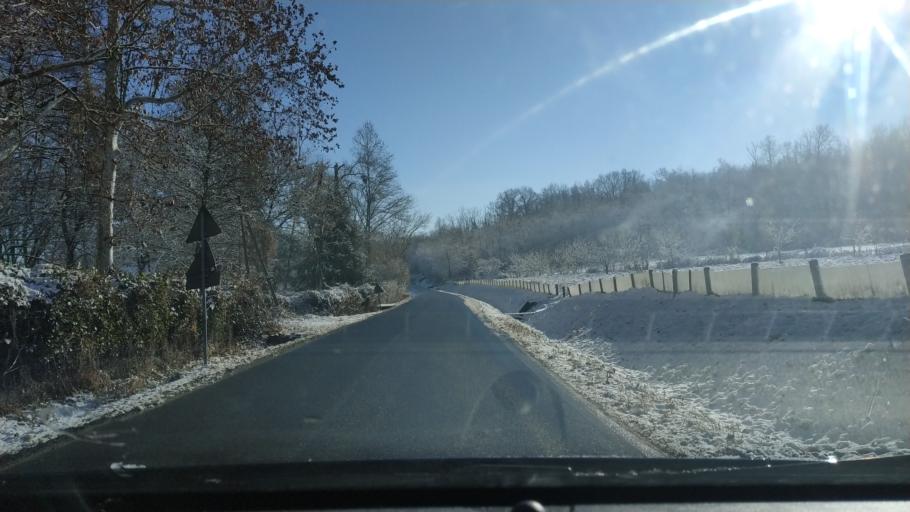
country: IT
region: Piedmont
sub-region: Provincia di Torino
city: Caluso
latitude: 45.3182
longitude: 7.9001
